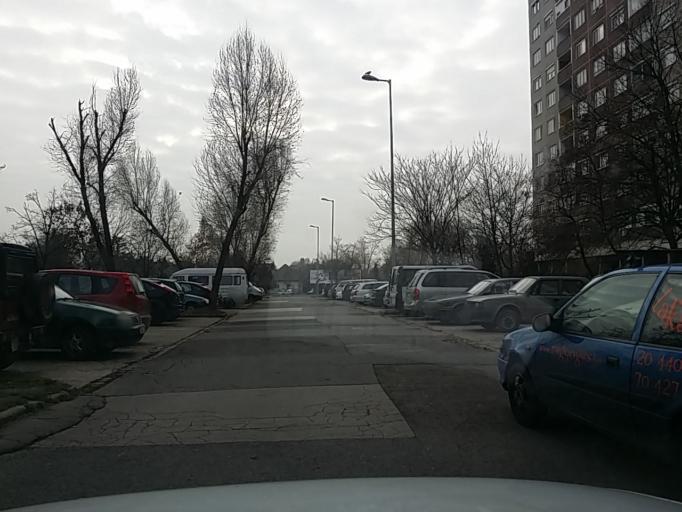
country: HU
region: Pest
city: Budakalasz
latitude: 47.5957
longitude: 19.0614
